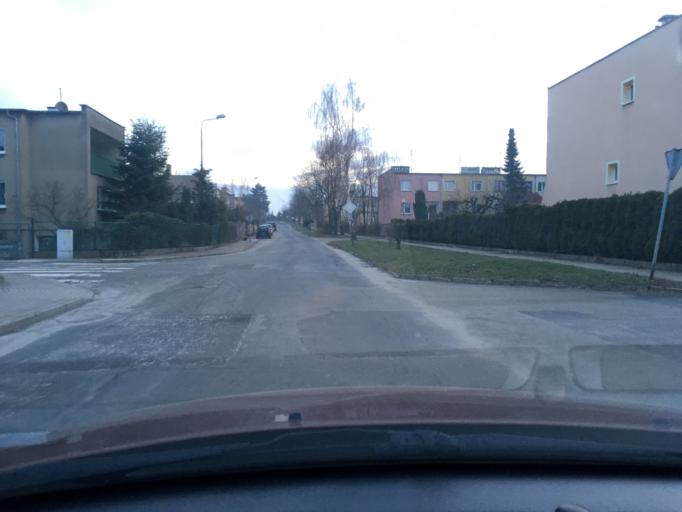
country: PL
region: Lower Silesian Voivodeship
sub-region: Powiat zgorzelecki
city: Zgorzelec
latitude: 51.1308
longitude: 15.0098
